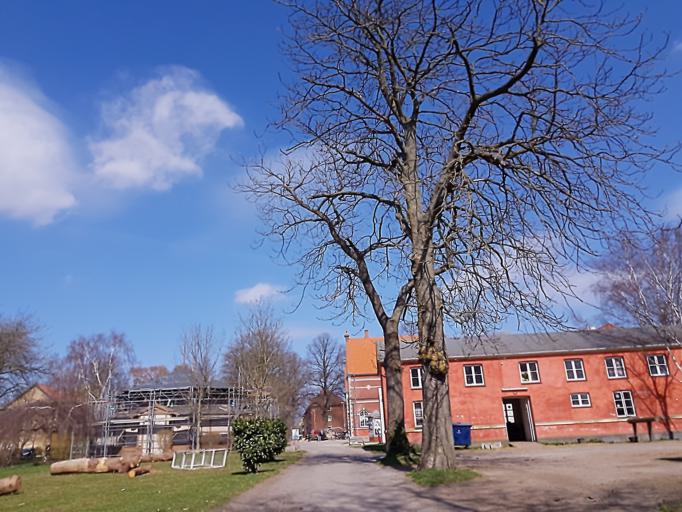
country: DK
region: Capital Region
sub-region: Frederiksberg Kommune
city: Frederiksberg
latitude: 55.6459
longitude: 12.5296
